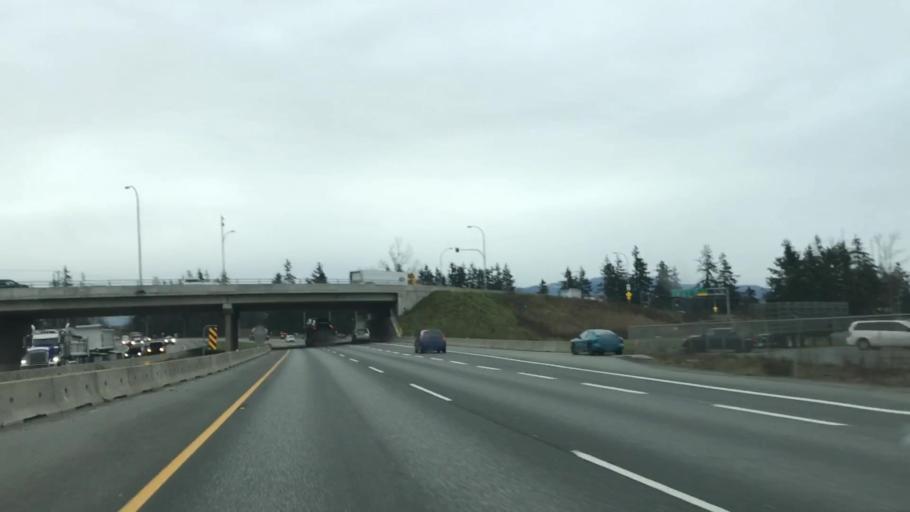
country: US
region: Washington
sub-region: Whatcom County
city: Sumas
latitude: 49.0383
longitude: -122.3390
